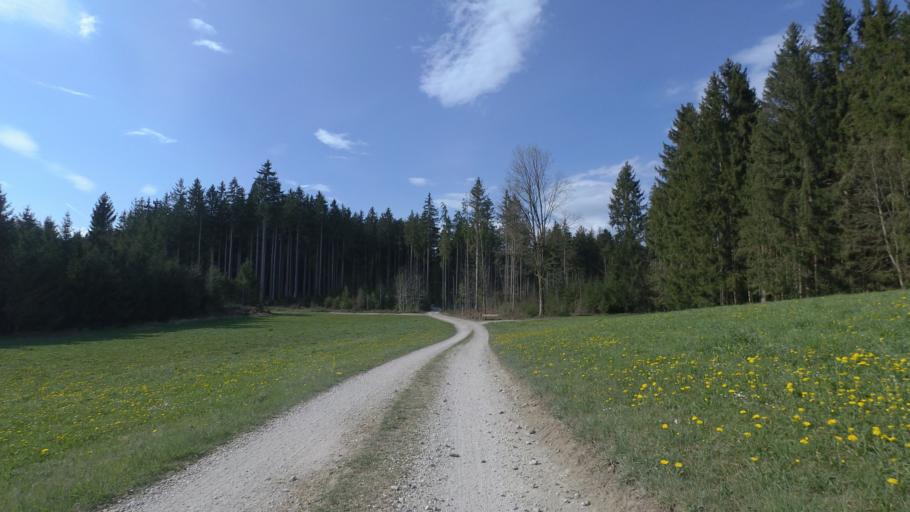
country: DE
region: Bavaria
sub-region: Upper Bavaria
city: Nussdorf
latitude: 47.9142
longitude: 12.5819
